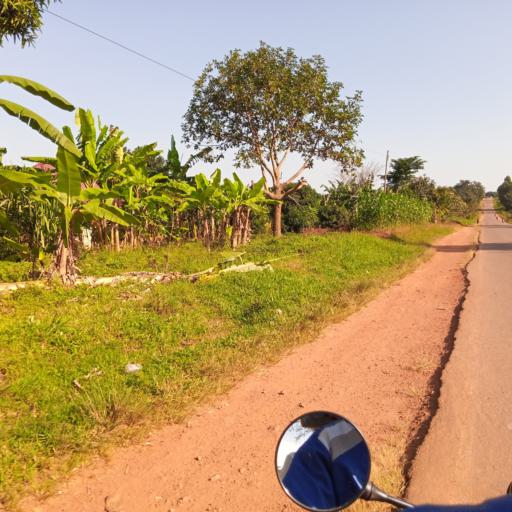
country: UG
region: Central Region
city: Masaka
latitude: -0.4427
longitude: 31.6655
